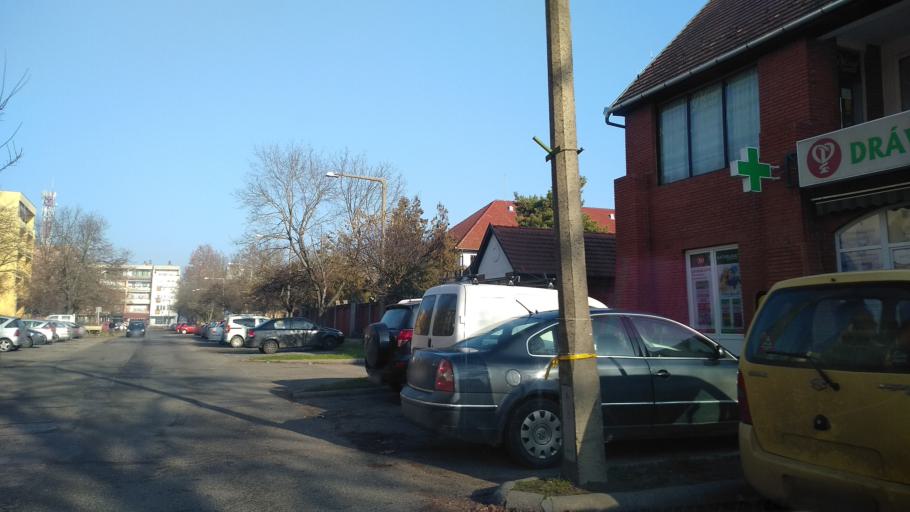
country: HU
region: Somogy
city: Barcs
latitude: 45.9594
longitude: 17.4625
